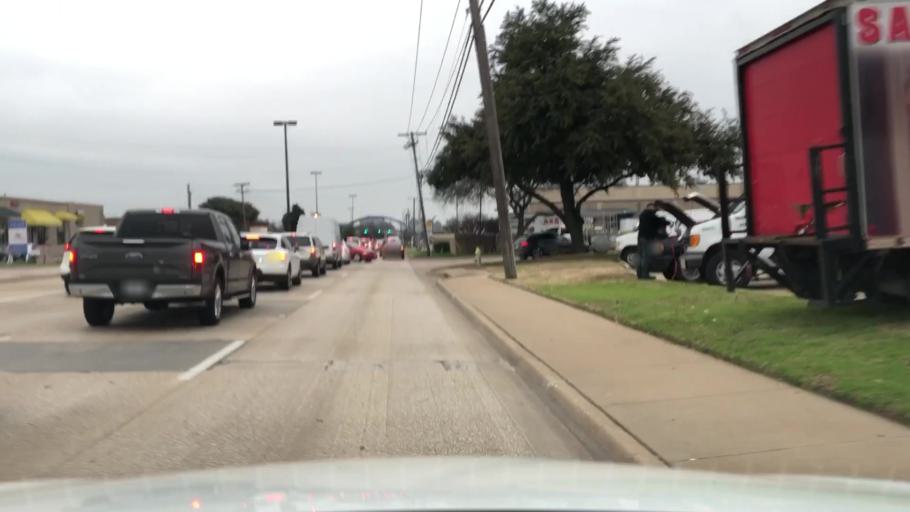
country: US
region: Texas
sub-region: Dallas County
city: Addison
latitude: 32.9606
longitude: -96.8386
